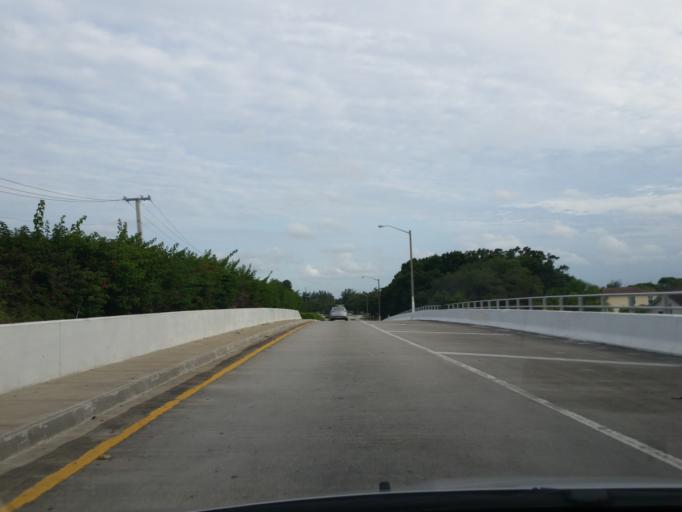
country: US
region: Florida
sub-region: Broward County
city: Broadview Park
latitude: 26.0683
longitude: -80.1827
